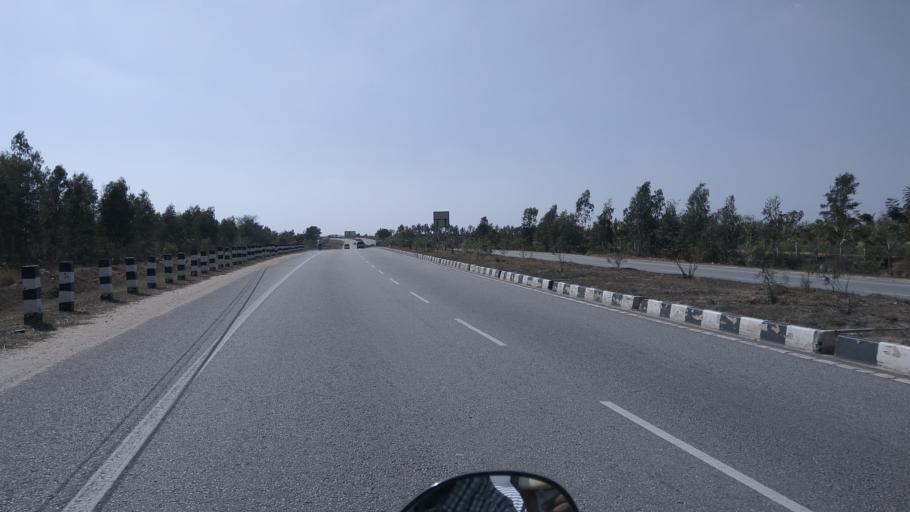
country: IN
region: Karnataka
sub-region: Kolar
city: Mulbagal
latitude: 13.1523
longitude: 78.3141
